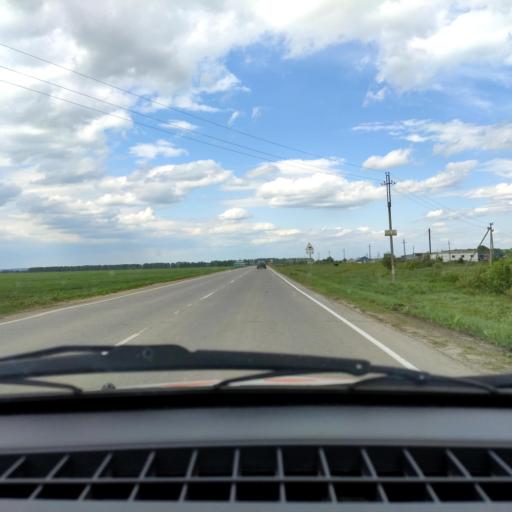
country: RU
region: Bashkortostan
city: Iglino
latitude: 54.9506
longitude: 56.4813
